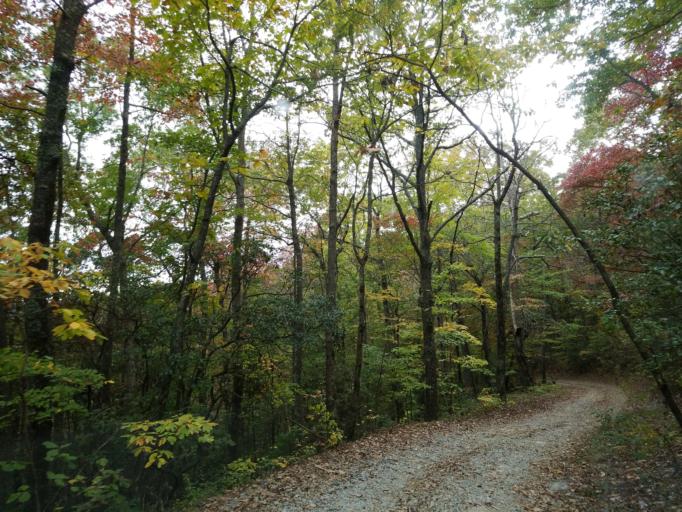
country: US
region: Georgia
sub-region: Dawson County
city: Dawsonville
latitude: 34.5910
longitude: -84.2207
